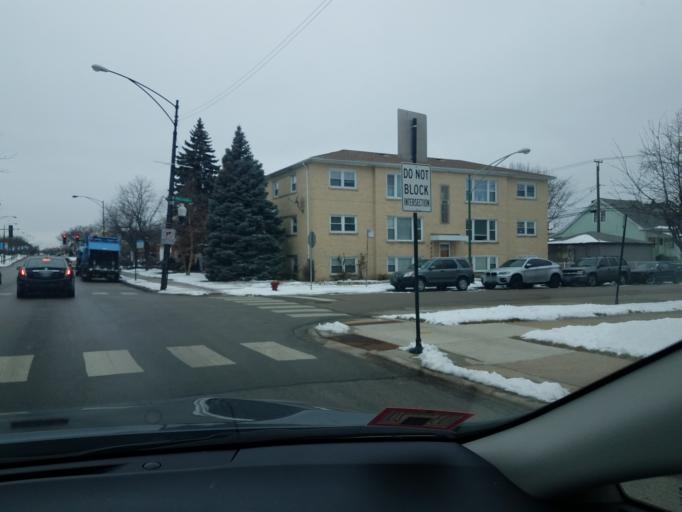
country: US
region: Illinois
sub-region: Cook County
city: Harwood Heights
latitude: 41.9603
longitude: -87.7854
